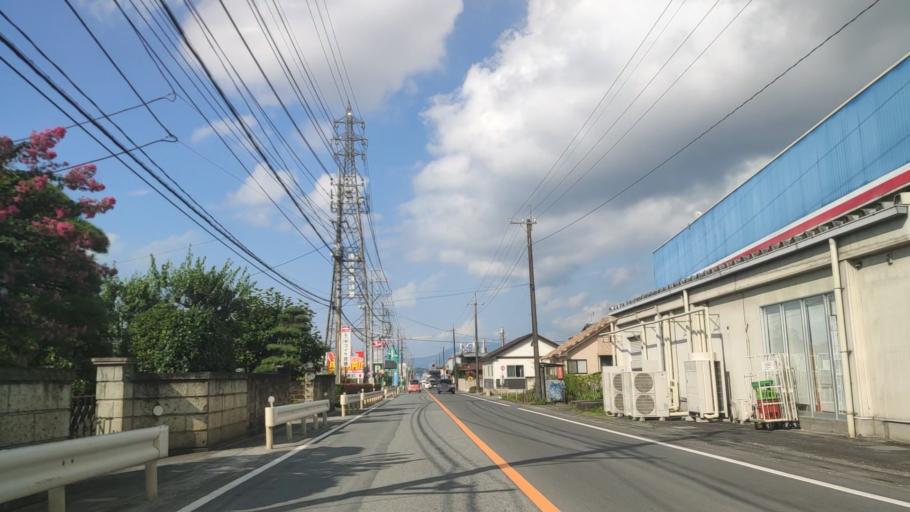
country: JP
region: Saitama
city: Chichibu
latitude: 35.9703
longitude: 139.0632
